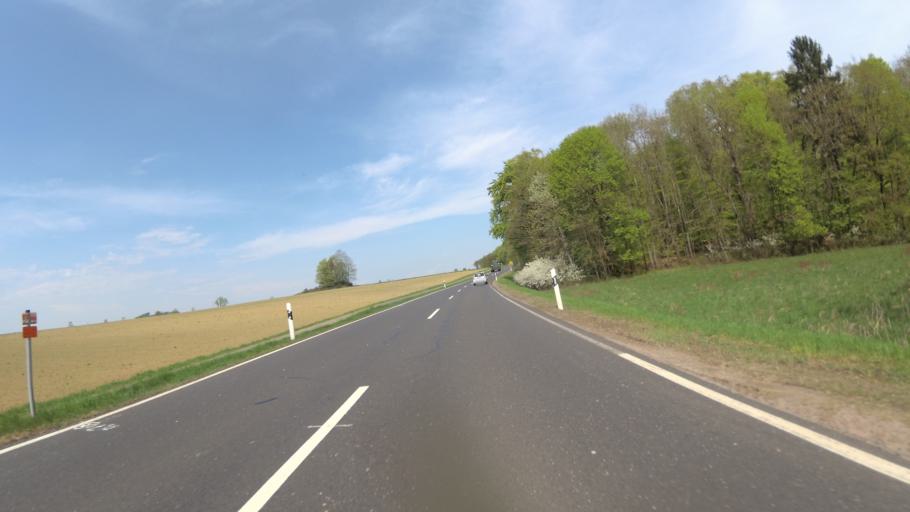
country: DE
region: Rheinland-Pfalz
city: Strotzbusch
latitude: 50.0932
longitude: 6.9678
